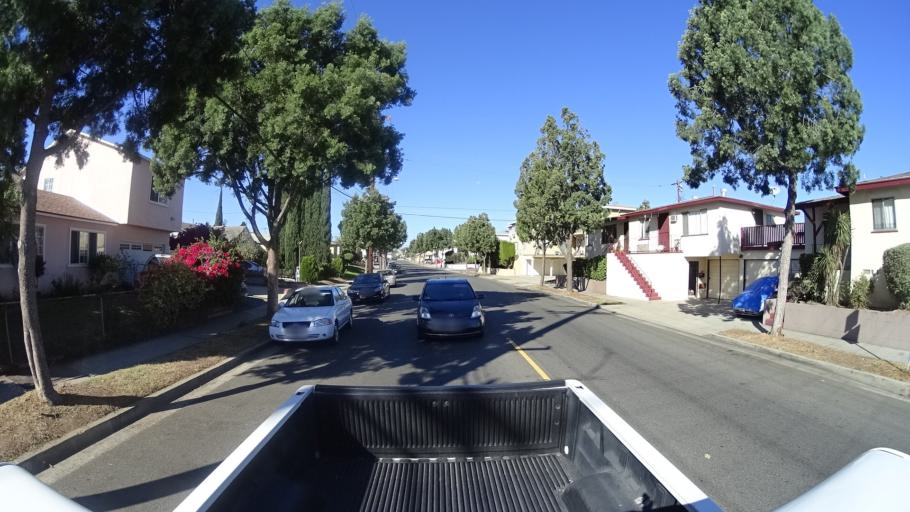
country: US
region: California
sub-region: Los Angeles County
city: Alhambra
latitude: 34.0875
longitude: -118.1397
